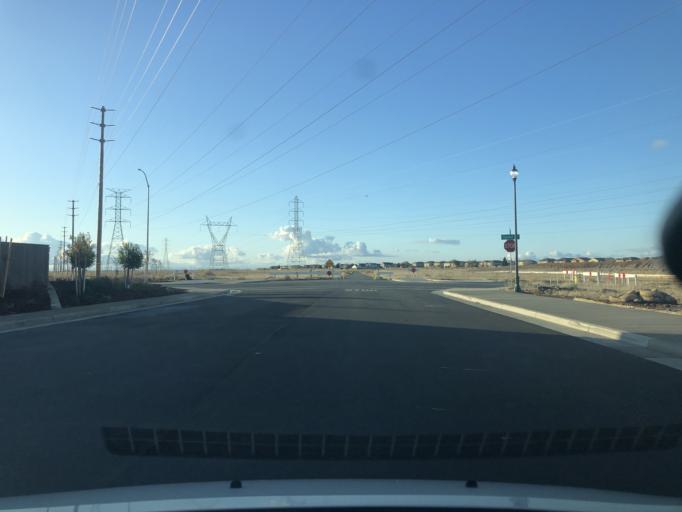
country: US
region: California
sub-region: Sacramento County
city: Antelope
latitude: 38.7636
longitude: -121.3638
